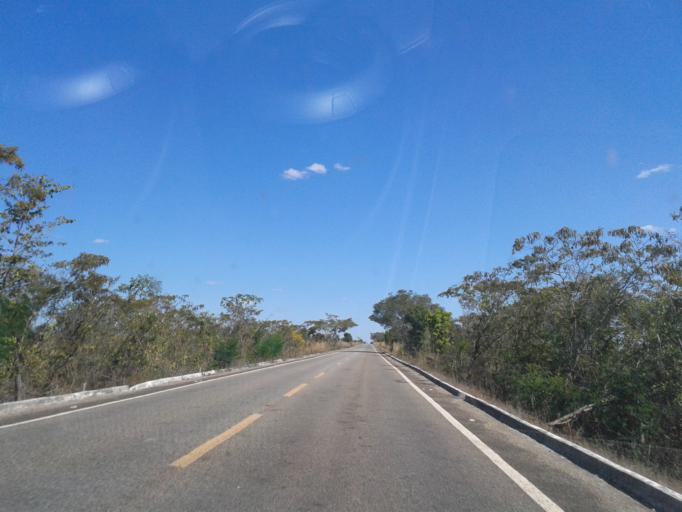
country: BR
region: Goias
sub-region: Sao Miguel Do Araguaia
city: Sao Miguel do Araguaia
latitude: -13.6354
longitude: -50.3136
